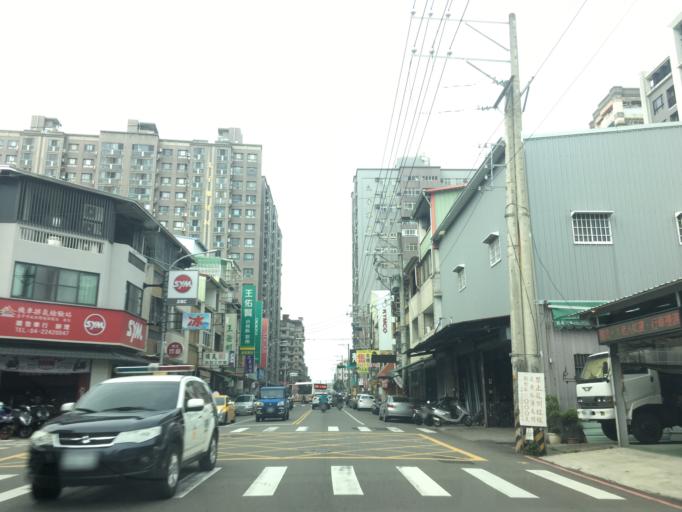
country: TW
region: Taiwan
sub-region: Taichung City
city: Taichung
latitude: 24.1823
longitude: 120.6951
